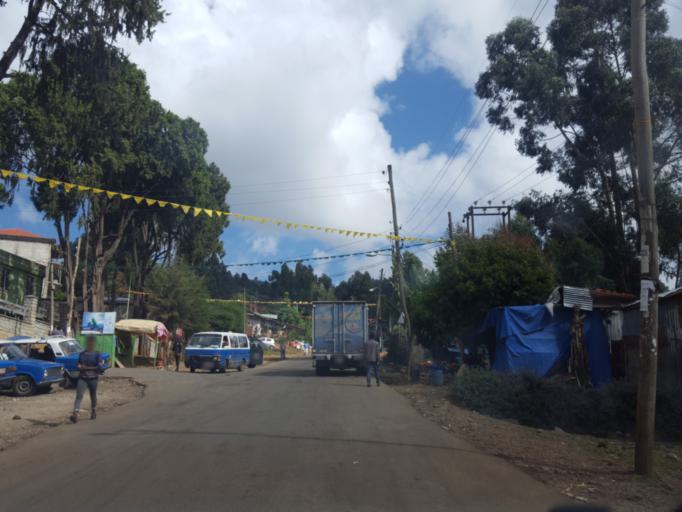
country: ET
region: Adis Abeba
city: Addis Ababa
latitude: 9.0741
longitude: 38.7590
